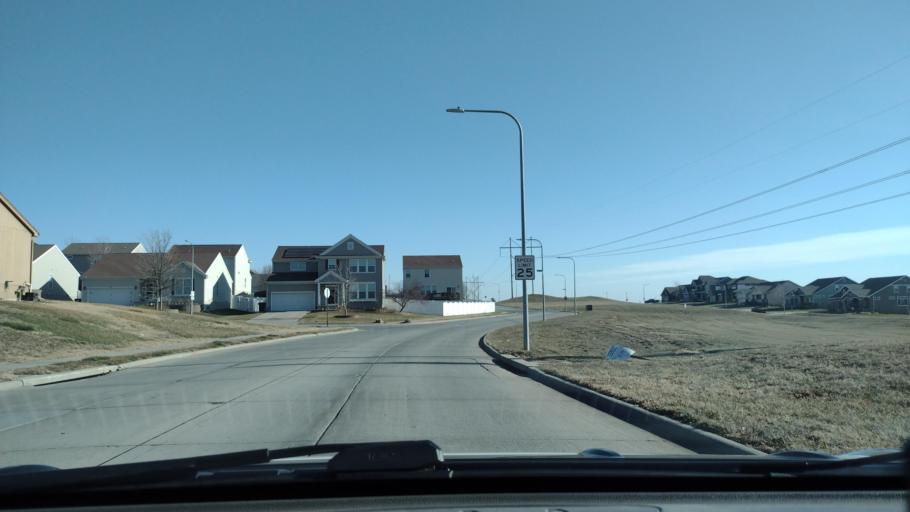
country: US
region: Nebraska
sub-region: Sarpy County
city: La Vista
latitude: 41.1696
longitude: -96.0177
